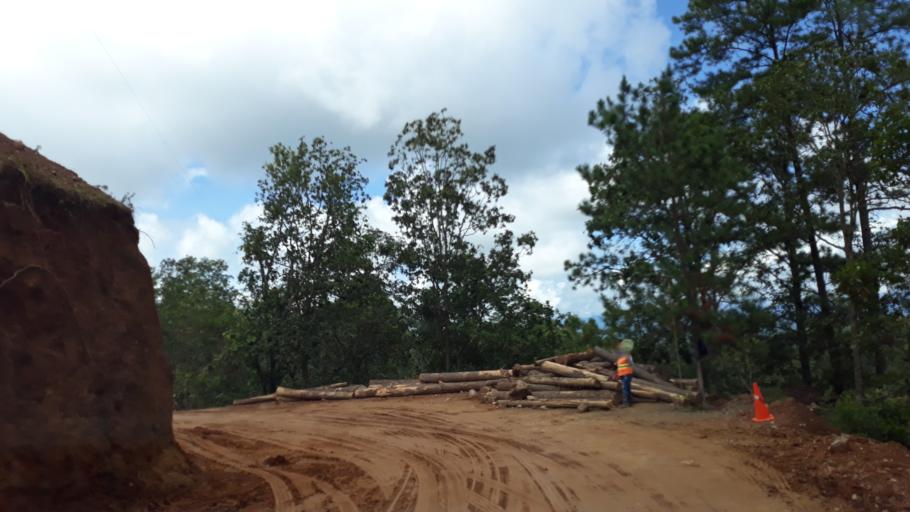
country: HN
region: El Paraiso
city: Santa Cruz
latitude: 13.7592
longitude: -86.6507
